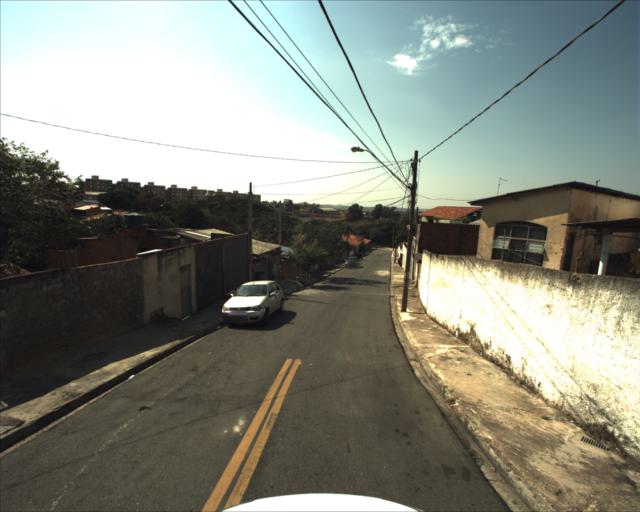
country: BR
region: Sao Paulo
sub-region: Sorocaba
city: Sorocaba
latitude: -23.4743
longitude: -47.4688
